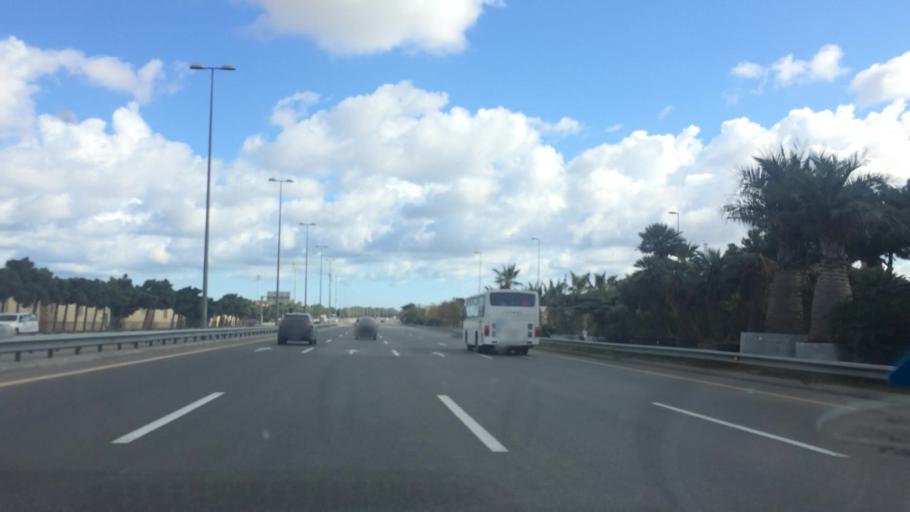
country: AZ
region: Baki
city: Biny Selo
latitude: 40.4602
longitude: 50.0775
